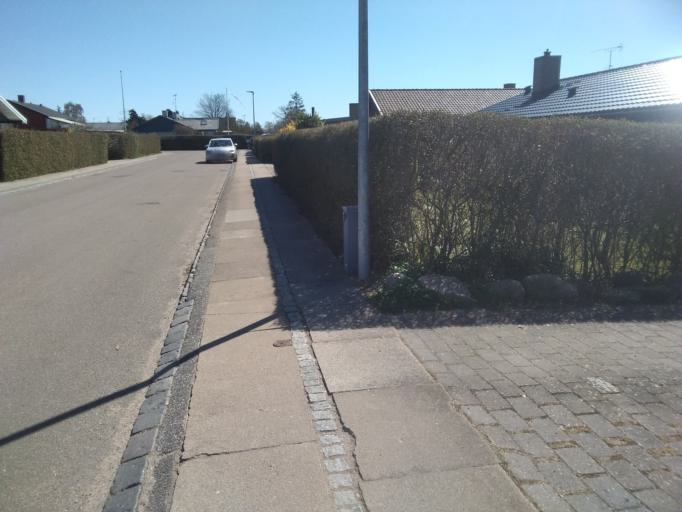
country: DK
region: Zealand
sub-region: Roskilde Kommune
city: Jyllinge
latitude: 55.7691
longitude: 12.1178
